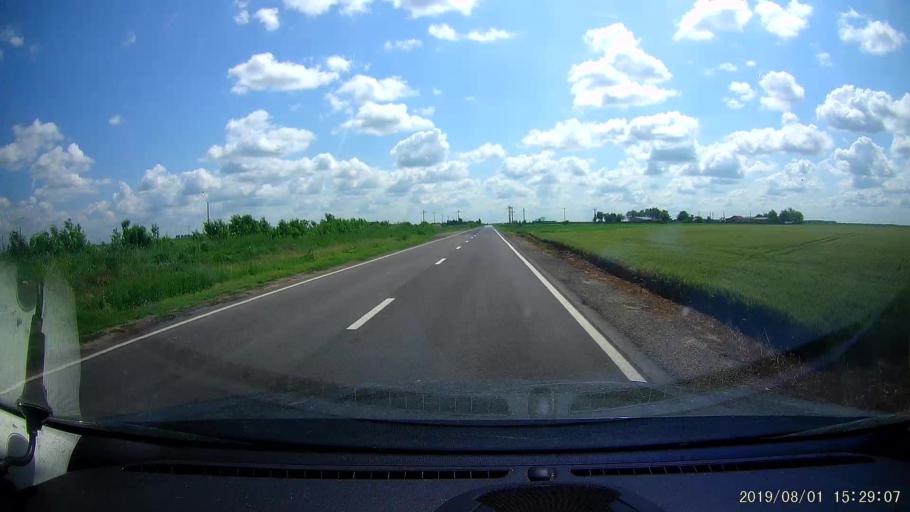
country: RO
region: Braila
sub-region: Comuna Viziru
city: Viziru
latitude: 44.9873
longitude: 27.7025
